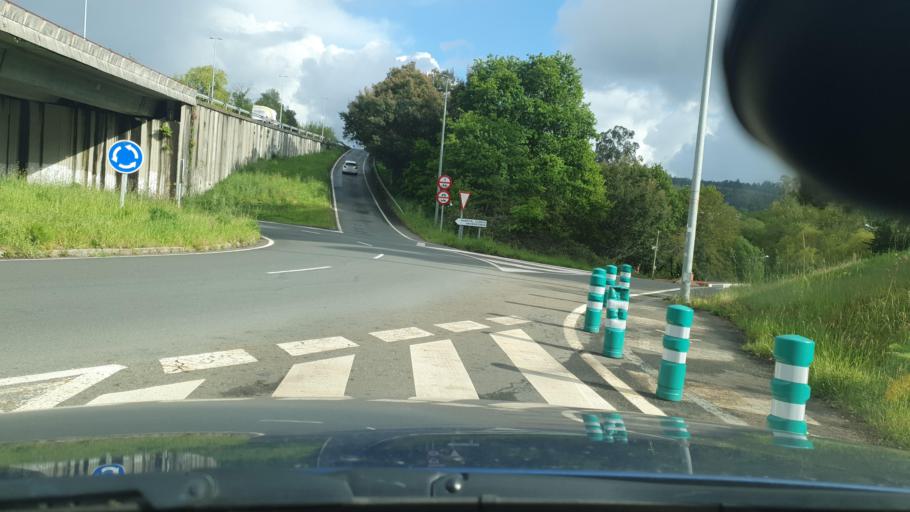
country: ES
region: Galicia
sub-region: Provincia da Coruna
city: Santiago de Compostela
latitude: 42.8669
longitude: -8.5717
